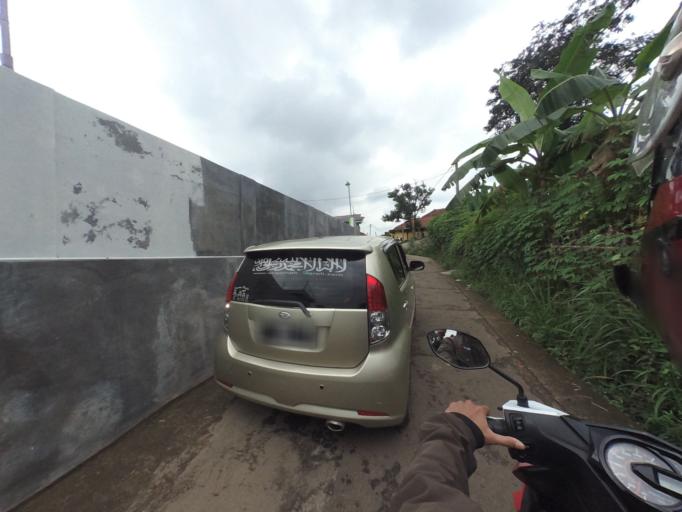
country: ID
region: West Java
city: Bogor
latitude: -6.6104
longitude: 106.7380
